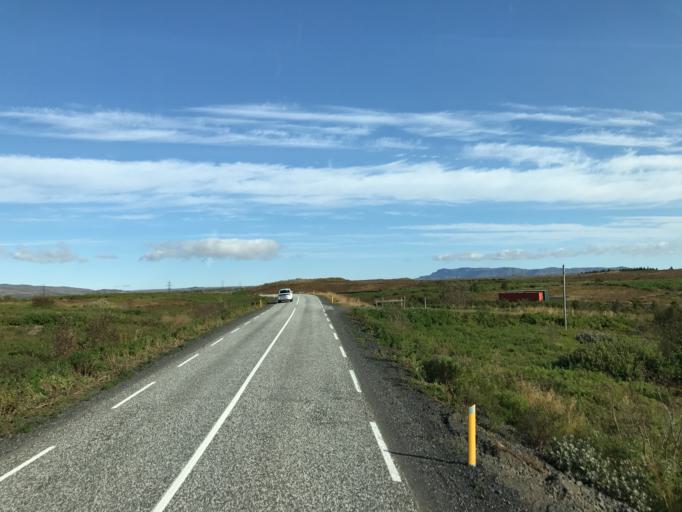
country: IS
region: Capital Region
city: Mosfellsbaer
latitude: 64.0948
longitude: -21.7056
